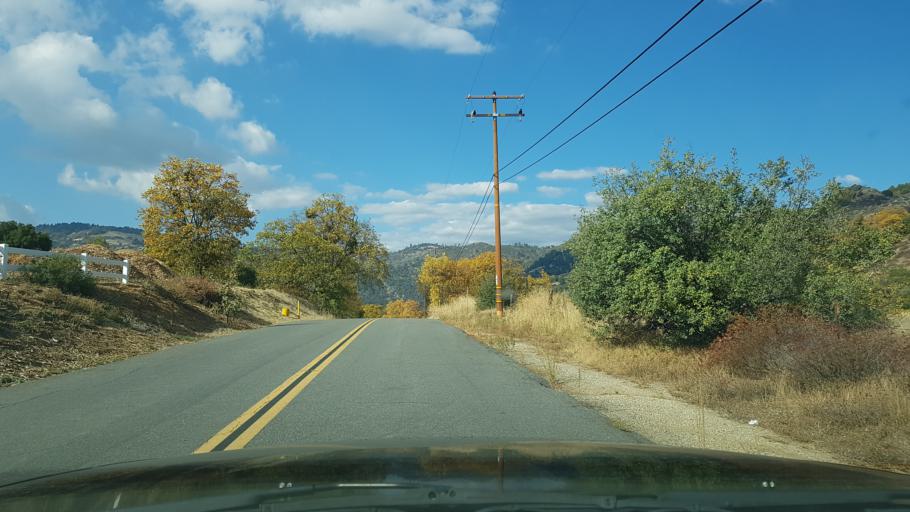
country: US
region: California
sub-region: San Diego County
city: Julian
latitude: 33.1069
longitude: -116.6025
